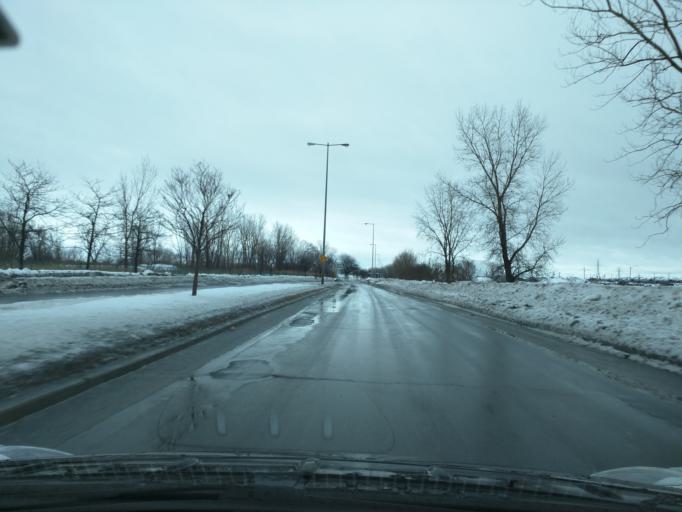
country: CA
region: Quebec
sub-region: Monteregie
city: Longueuil
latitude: 45.5060
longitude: -73.4833
